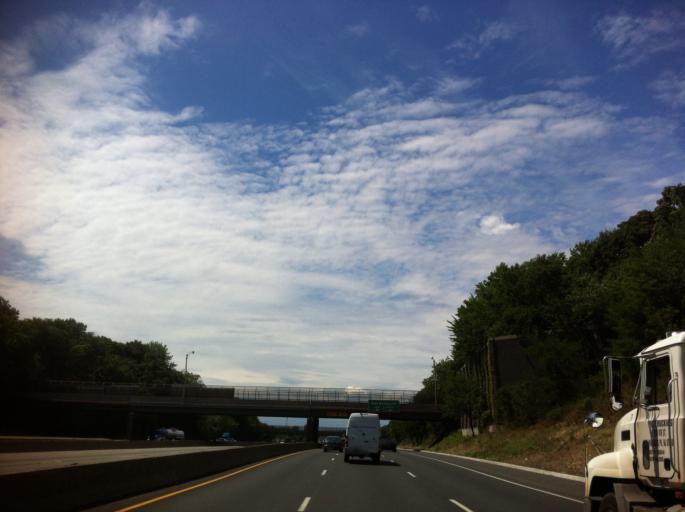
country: US
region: New Jersey
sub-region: Bergen County
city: Ridgefield Park
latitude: 40.8656
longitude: -74.0170
